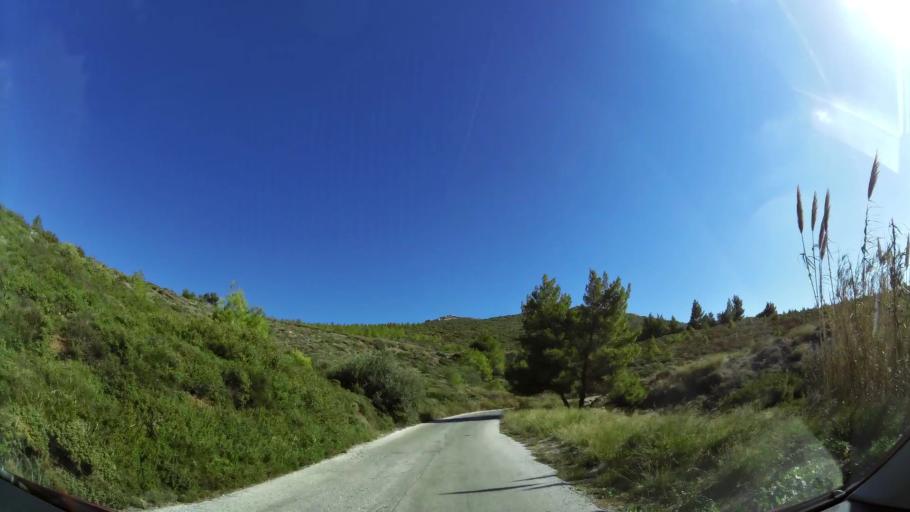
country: GR
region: Attica
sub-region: Nomarchia Anatolikis Attikis
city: Dhrafi
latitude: 38.0414
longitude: 23.9151
